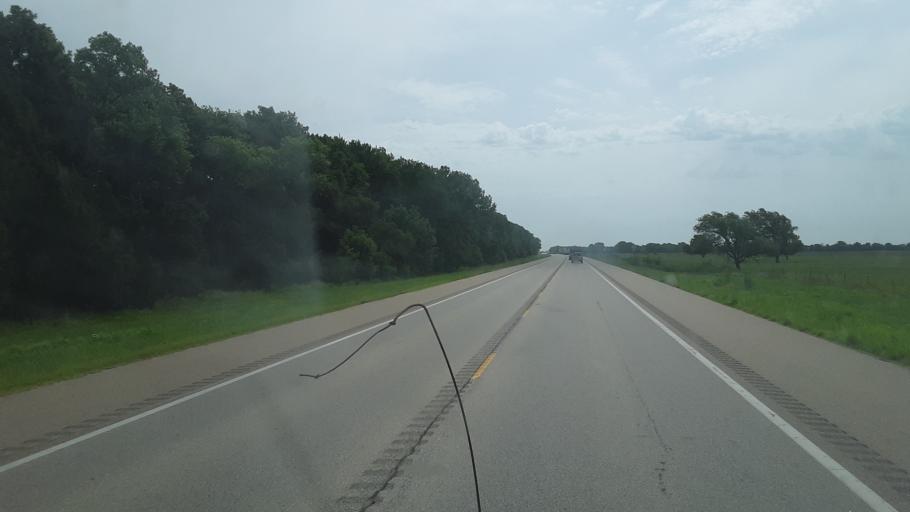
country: US
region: Kansas
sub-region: Rice County
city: Sterling
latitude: 37.9846
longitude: -98.2492
